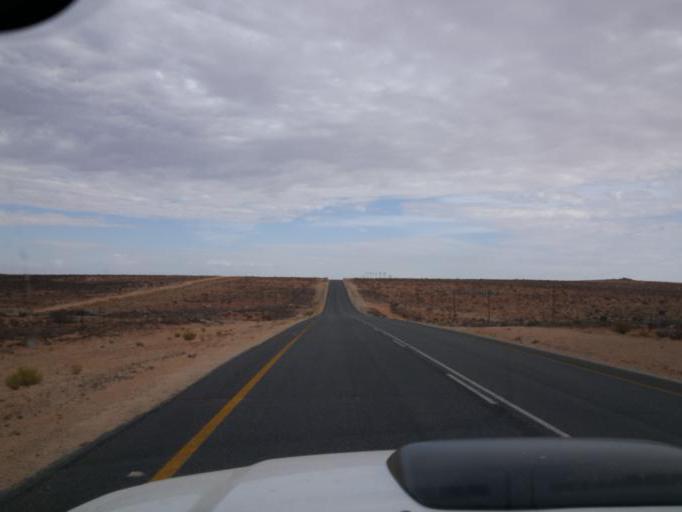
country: ZA
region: Northern Cape
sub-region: Namakwa District Municipality
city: Springbok
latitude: -29.4039
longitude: 17.8105
